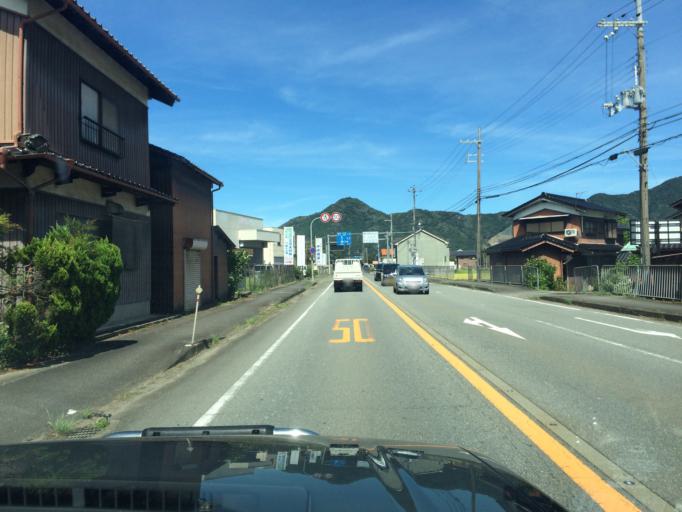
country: JP
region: Hyogo
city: Toyooka
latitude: 35.4212
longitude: 134.7905
